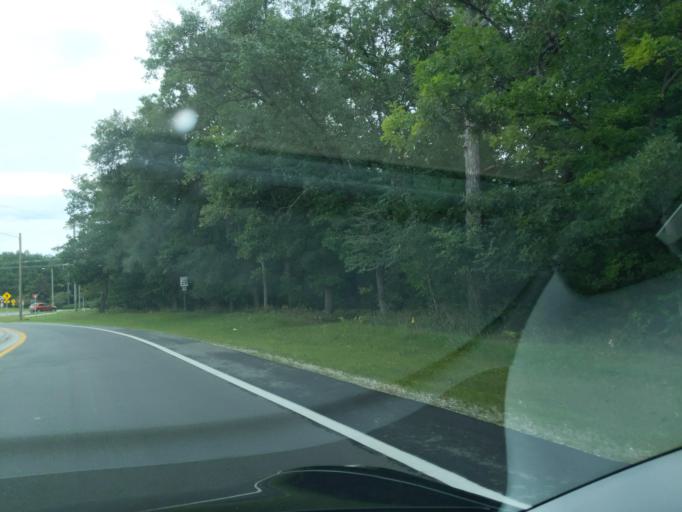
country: US
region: Michigan
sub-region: Grand Traverse County
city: Traverse City
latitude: 44.7528
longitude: -85.5810
